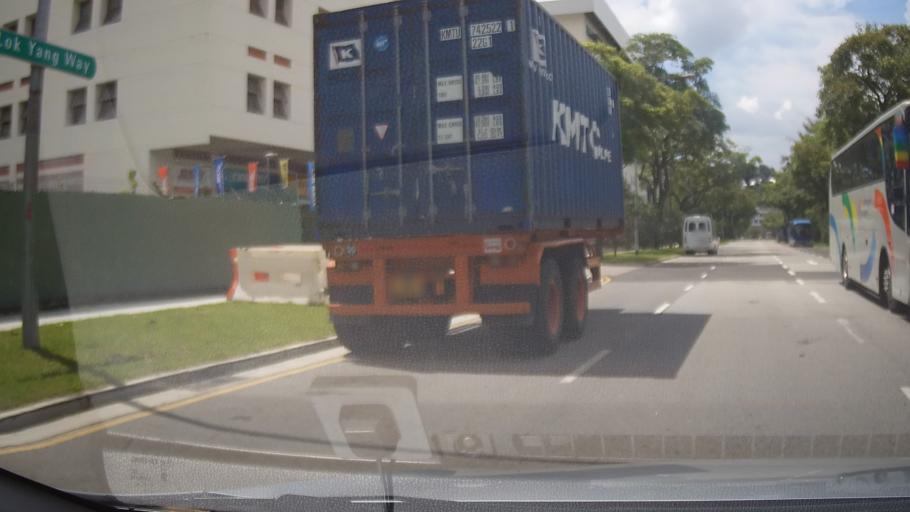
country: MY
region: Johor
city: Johor Bahru
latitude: 1.3246
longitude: 103.6882
